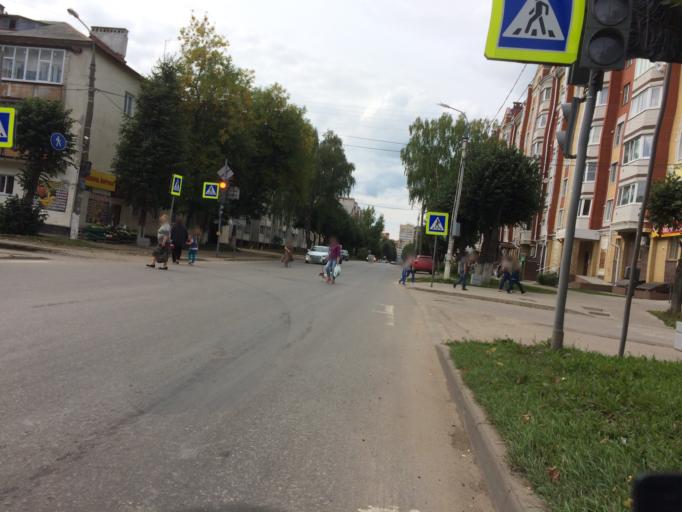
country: RU
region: Mariy-El
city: Yoshkar-Ola
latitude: 56.6355
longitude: 47.8708
